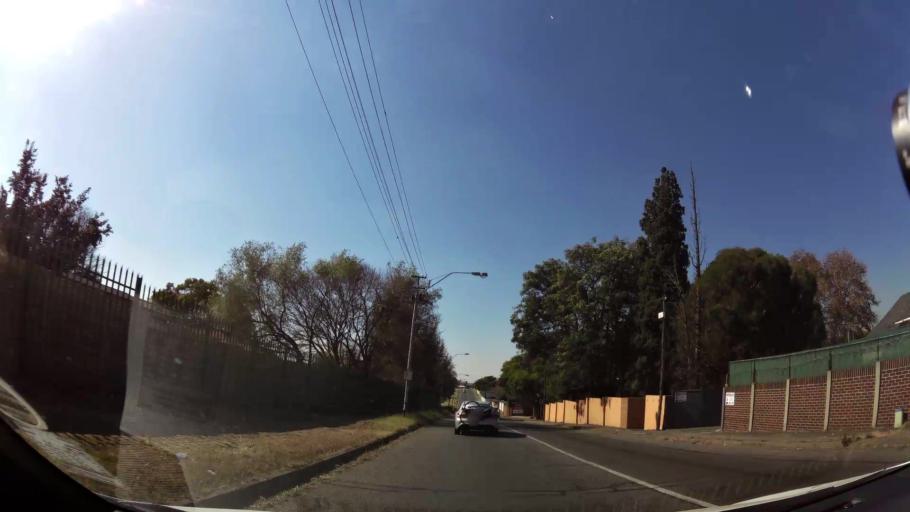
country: ZA
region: Gauteng
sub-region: City of Johannesburg Metropolitan Municipality
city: Johannesburg
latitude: -26.2580
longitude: 28.0443
